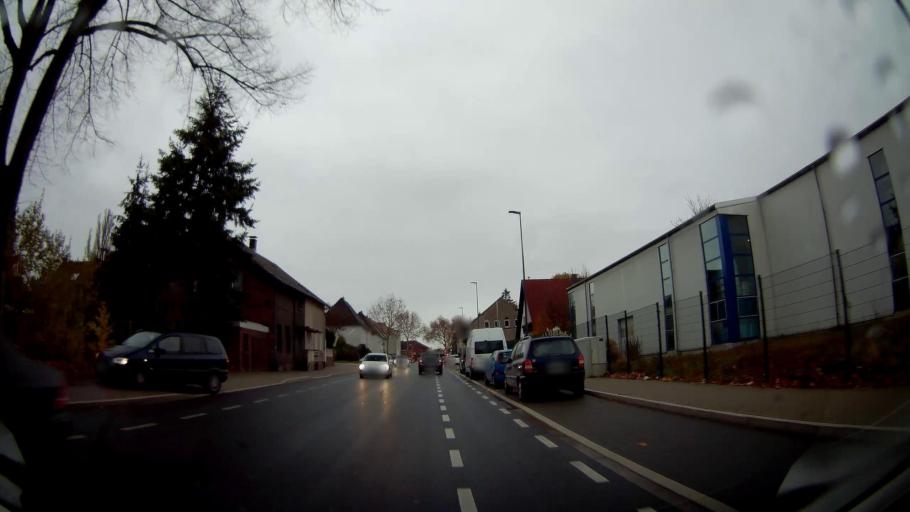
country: DE
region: North Rhine-Westphalia
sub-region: Regierungsbezirk Munster
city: Gelsenkirchen
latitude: 51.4862
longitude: 7.0833
